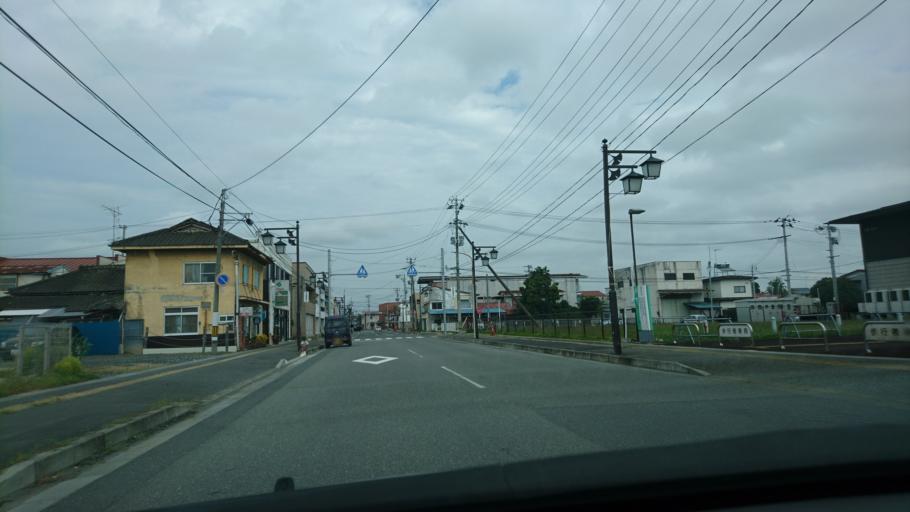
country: JP
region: Miyagi
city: Furukawa
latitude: 38.7328
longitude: 141.0262
